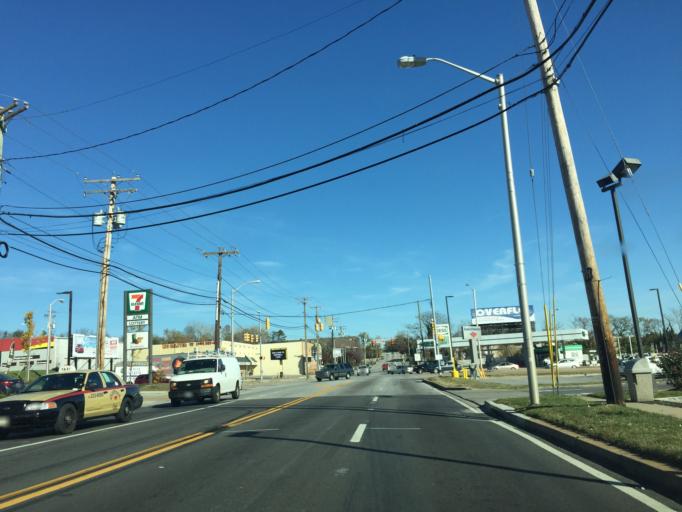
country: US
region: Maryland
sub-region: Baltimore County
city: Lansdowne
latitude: 39.2572
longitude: -76.6642
